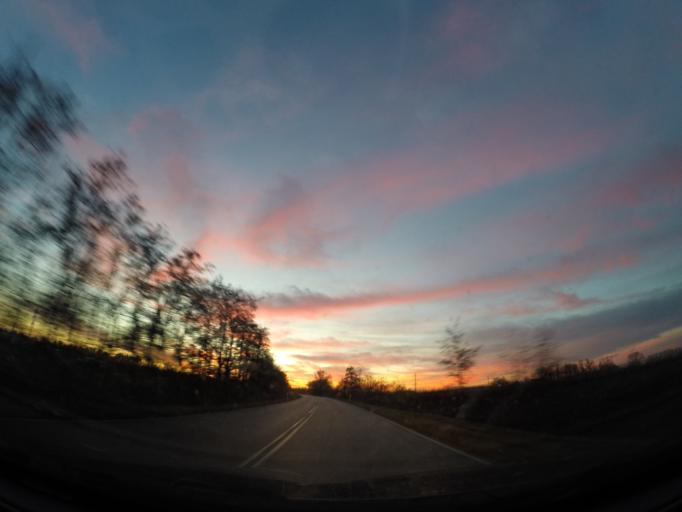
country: DK
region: Capital Region
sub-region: Hoje-Taastrup Kommune
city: Taastrup
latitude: 55.6731
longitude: 12.3005
